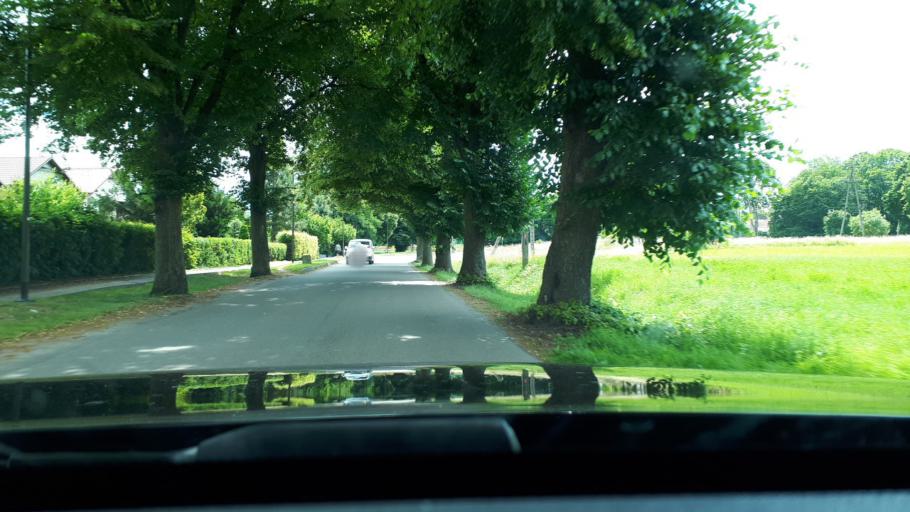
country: PL
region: Warmian-Masurian Voivodeship
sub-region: Powiat olsztynski
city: Olsztynek
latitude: 53.5866
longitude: 20.2827
